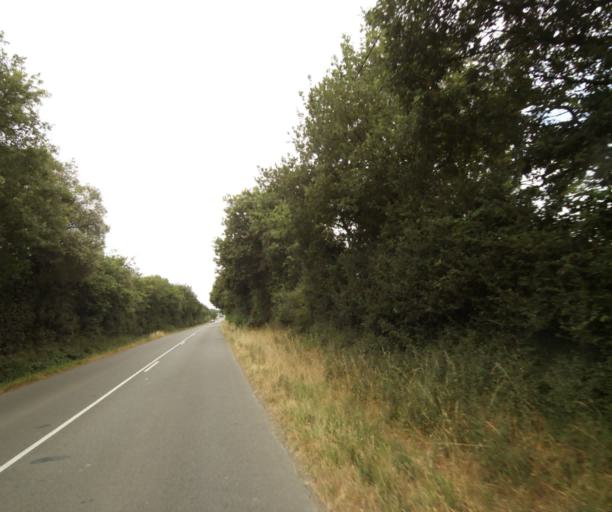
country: FR
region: Pays de la Loire
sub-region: Departement de la Vendee
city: Sainte-Foy
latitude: 46.5116
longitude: -1.6973
